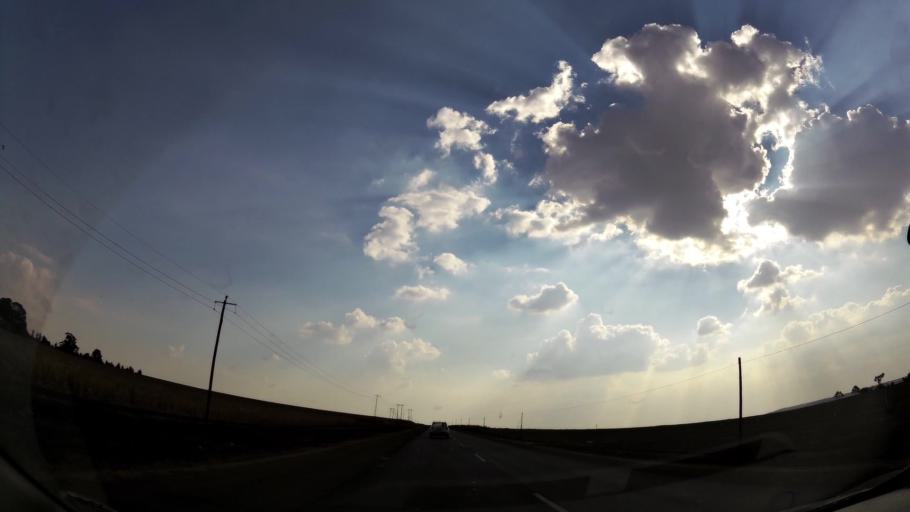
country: ZA
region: Gauteng
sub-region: Sedibeng District Municipality
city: Heidelberg
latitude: -26.3872
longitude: 28.3335
